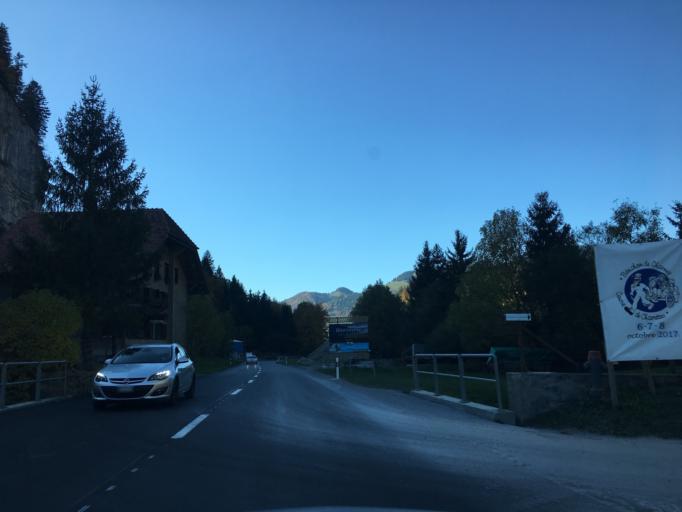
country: CH
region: Fribourg
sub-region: Gruyere District
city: Charmey
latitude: 46.6103
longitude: 7.1816
